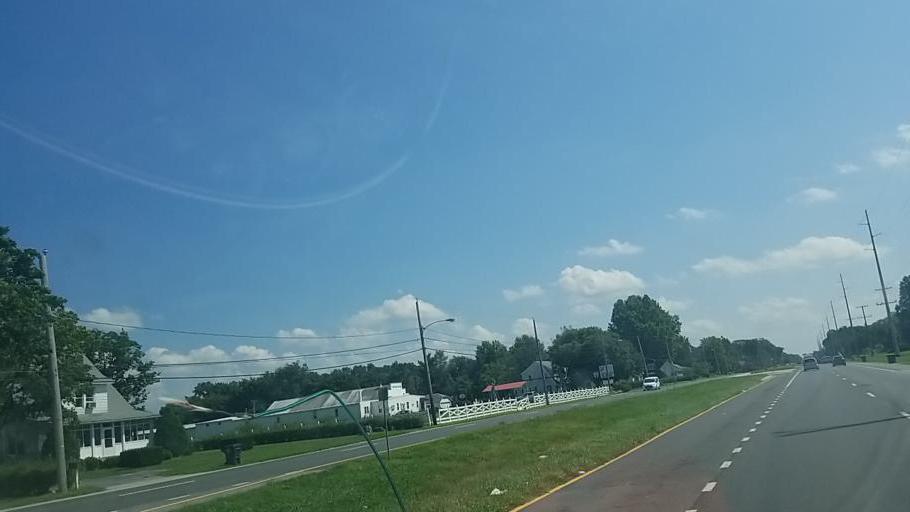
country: US
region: Delaware
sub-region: Sussex County
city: Milford
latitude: 38.8959
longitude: -75.4397
